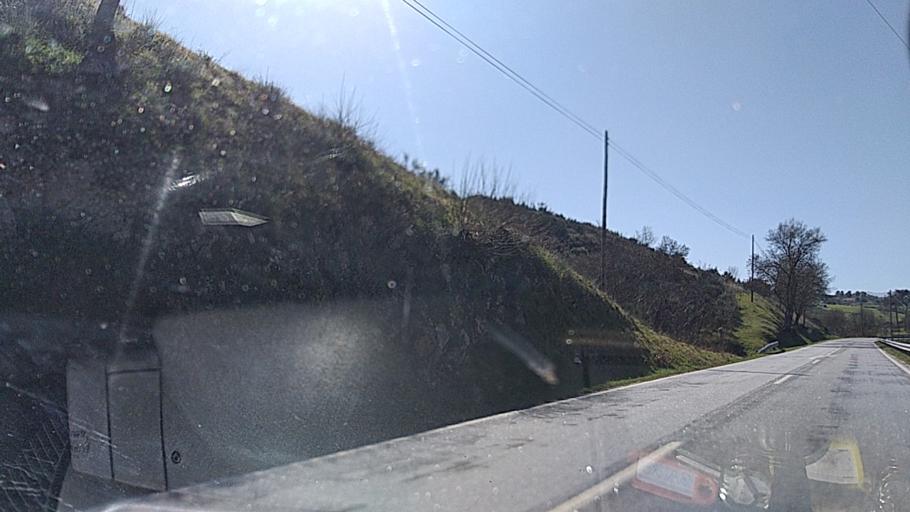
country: PT
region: Guarda
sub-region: Celorico da Beira
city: Celorico da Beira
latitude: 40.6026
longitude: -7.4239
